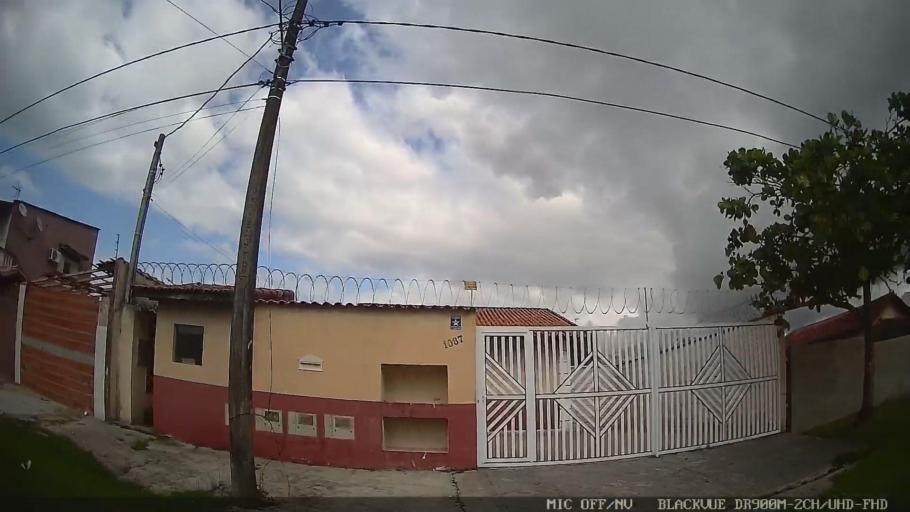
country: BR
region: Sao Paulo
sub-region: Itanhaem
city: Itanhaem
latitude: -24.2007
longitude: -46.8391
